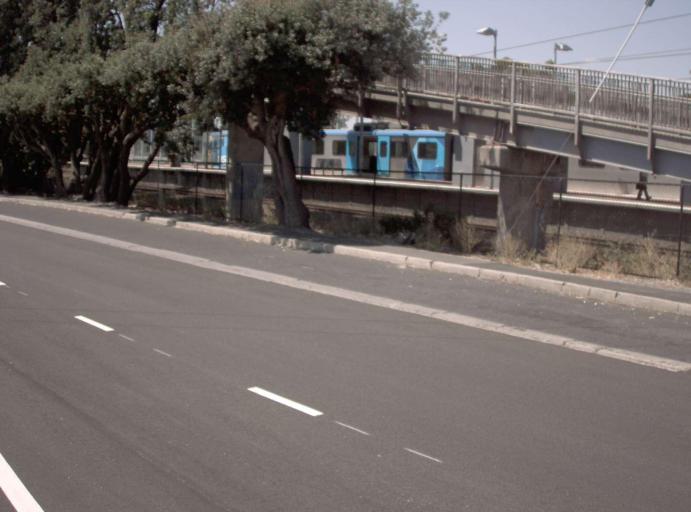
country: AU
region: Victoria
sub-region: Frankston
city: Frankston East
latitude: -38.1215
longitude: 145.1351
